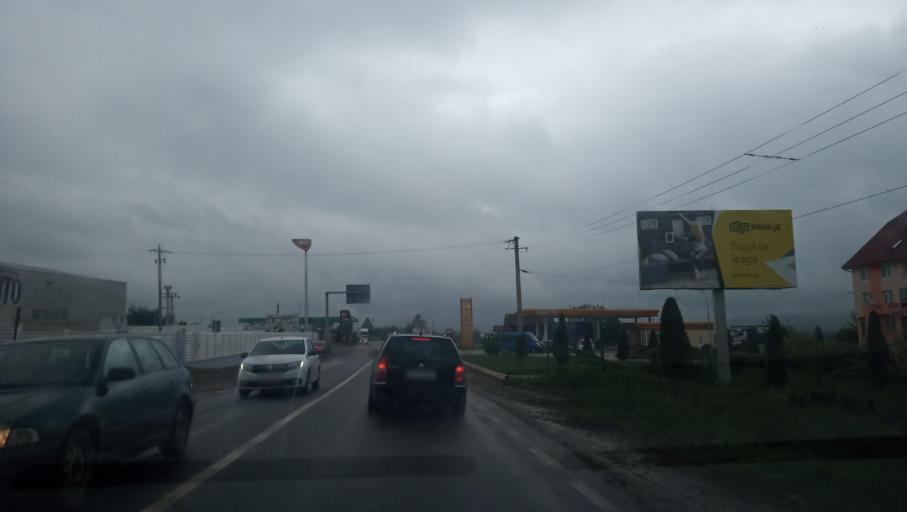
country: RO
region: Alba
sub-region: Municipiul Sebes
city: Sebes
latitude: 45.9468
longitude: 23.5874
